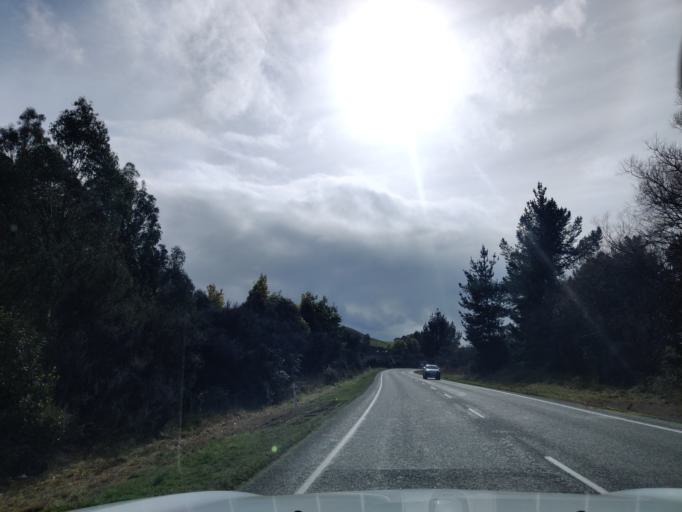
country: NZ
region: Manawatu-Wanganui
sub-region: Ruapehu District
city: Waiouru
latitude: -39.7568
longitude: 175.8291
